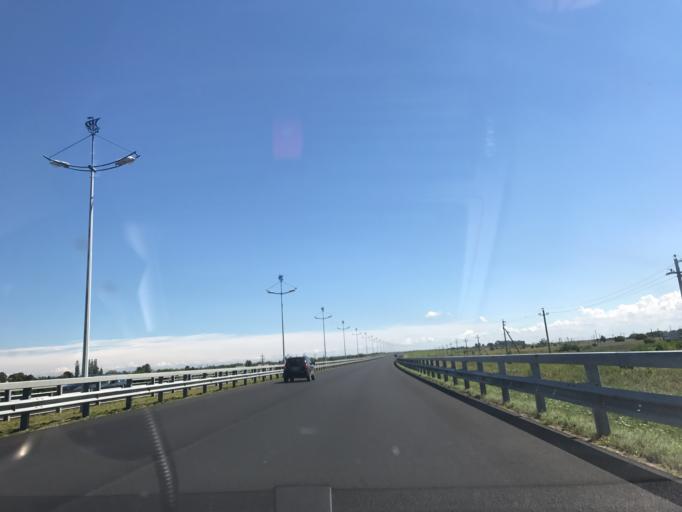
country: RU
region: Kaliningrad
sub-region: Zelenogradskiy Rayon
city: Zelenogradsk
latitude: 54.9194
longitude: 20.4677
